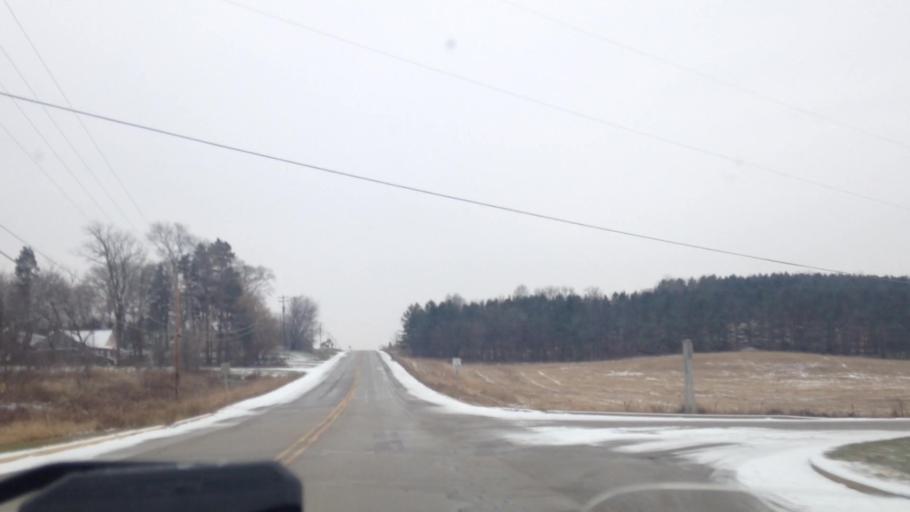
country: US
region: Wisconsin
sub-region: Dodge County
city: Hustisford
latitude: 43.3066
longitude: -88.5184
